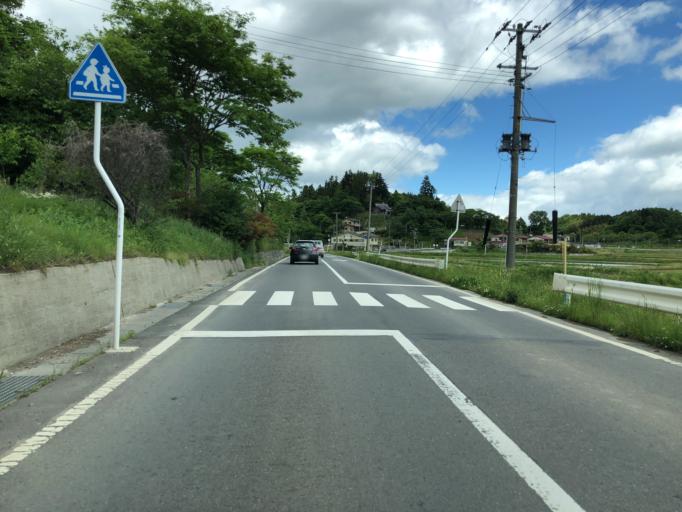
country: JP
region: Fukushima
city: Motomiya
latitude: 37.5170
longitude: 140.4734
